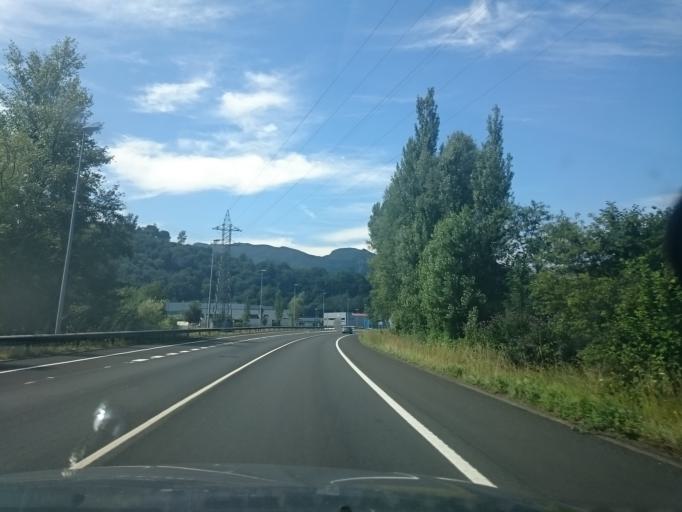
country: ES
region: Asturias
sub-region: Province of Asturias
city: Oviedo
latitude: 43.3099
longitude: -5.8227
